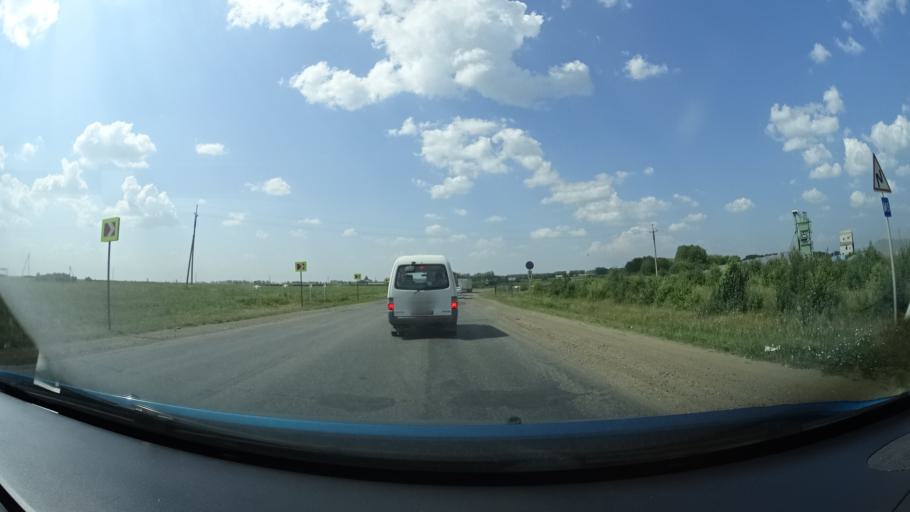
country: RU
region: Bashkortostan
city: Buzdyak
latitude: 54.6265
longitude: 54.4552
